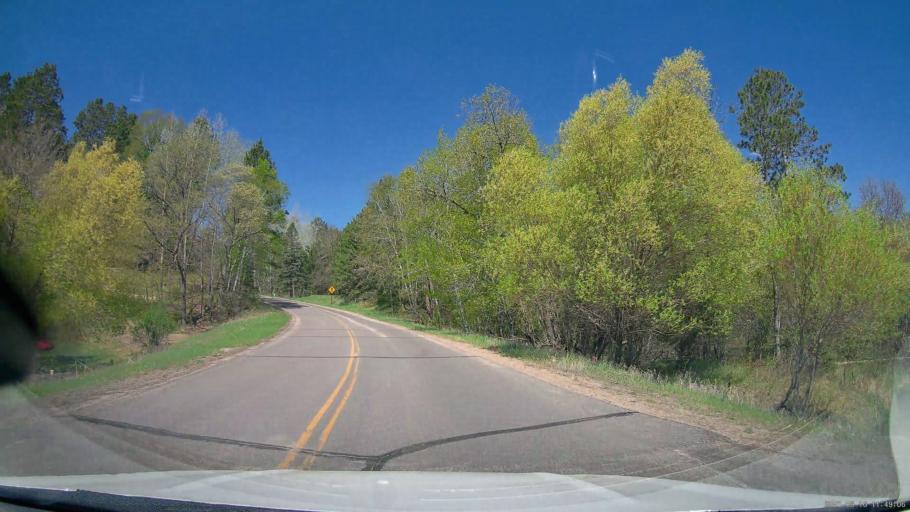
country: US
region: Minnesota
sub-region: Hubbard County
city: Park Rapids
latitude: 46.9861
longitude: -94.9493
